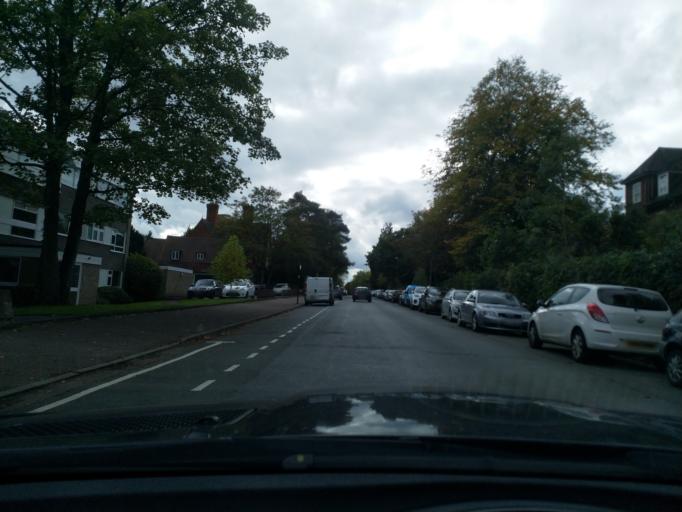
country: GB
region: England
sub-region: City and Borough of Birmingham
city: Birmingham
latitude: 52.4570
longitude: -1.9305
